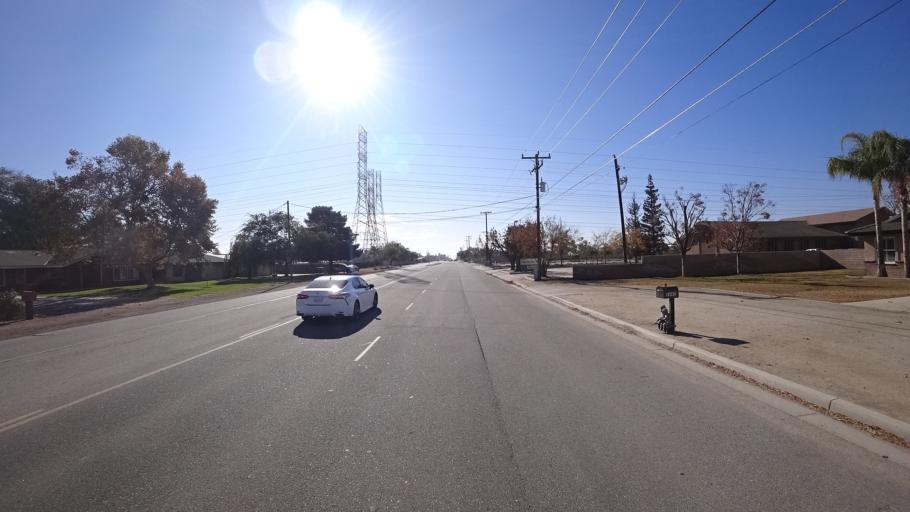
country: US
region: California
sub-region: Kern County
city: Rosedale
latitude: 35.3879
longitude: -119.1456
